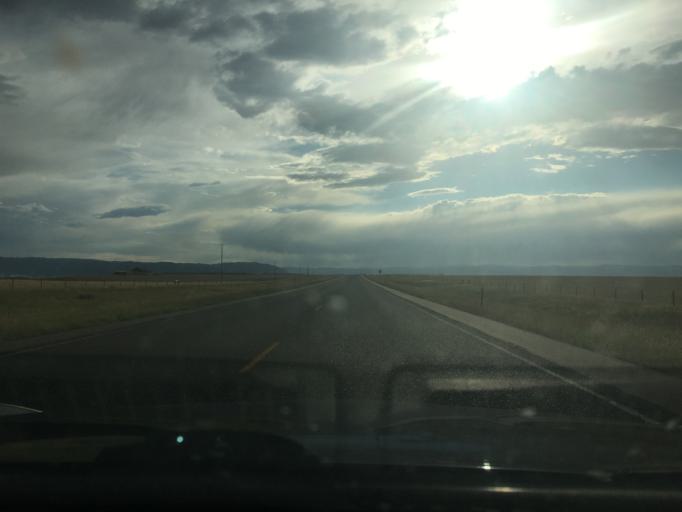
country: US
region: Wyoming
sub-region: Albany County
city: Laramie
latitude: 41.3115
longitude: -105.7941
